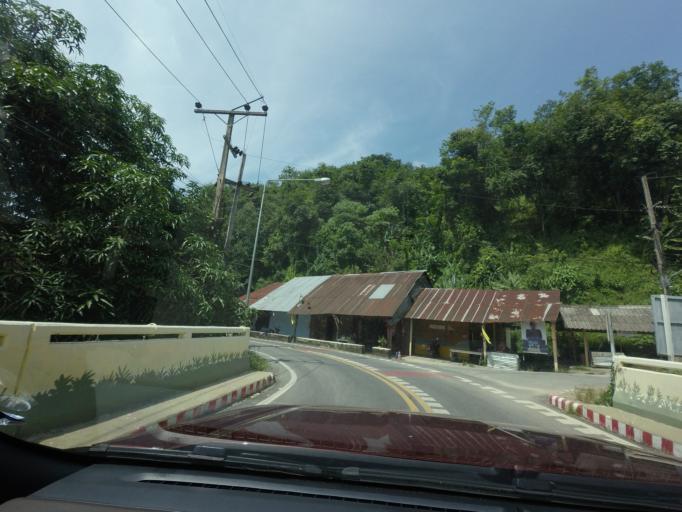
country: TH
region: Yala
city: Betong
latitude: 5.8361
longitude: 101.0750
